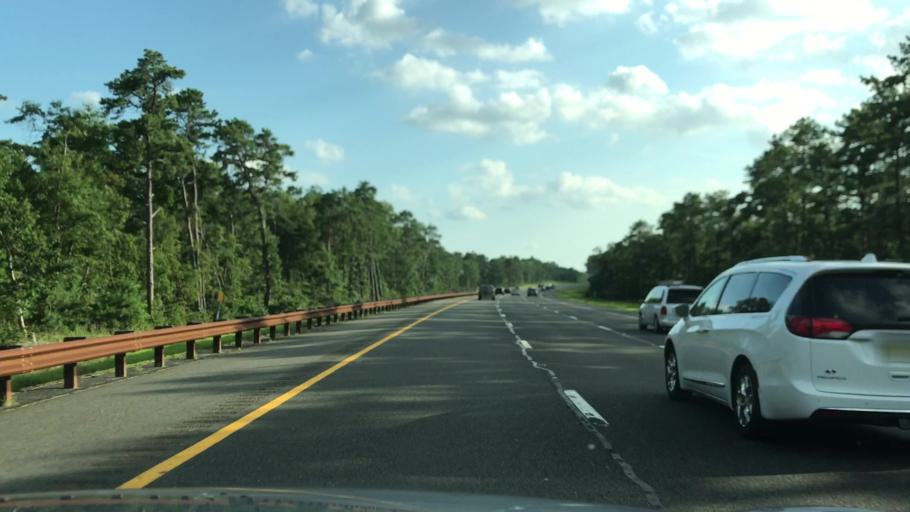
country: US
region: New Jersey
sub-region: Ocean County
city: Manahawkin
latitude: 39.6831
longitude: -74.3041
